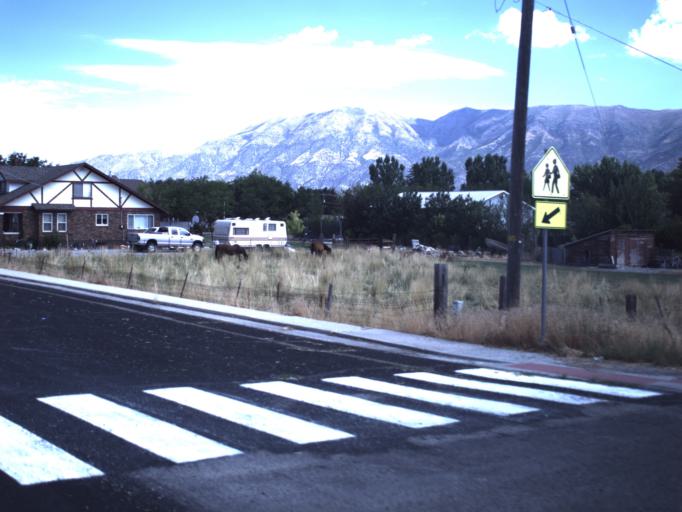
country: US
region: Utah
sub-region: Box Elder County
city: Honeyville
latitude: 41.6145
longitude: -112.1270
